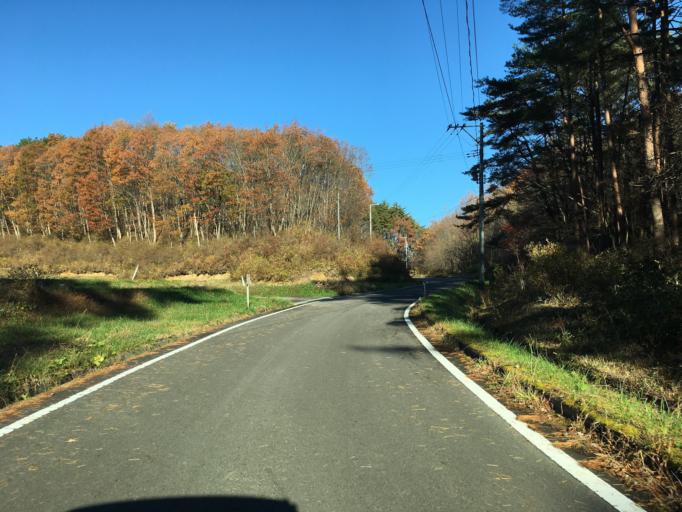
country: JP
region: Fukushima
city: Ishikawa
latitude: 37.2386
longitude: 140.5239
